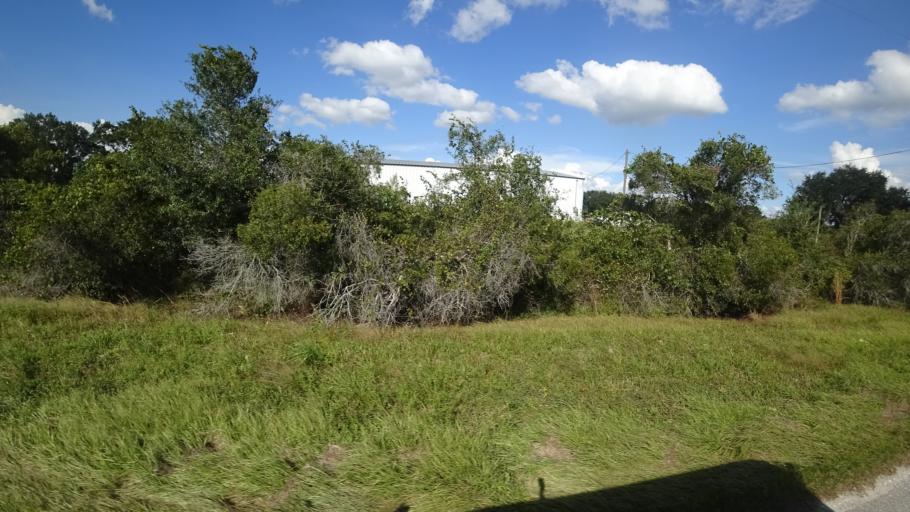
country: US
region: Florida
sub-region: DeSoto County
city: Nocatee
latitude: 27.2718
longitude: -82.1024
